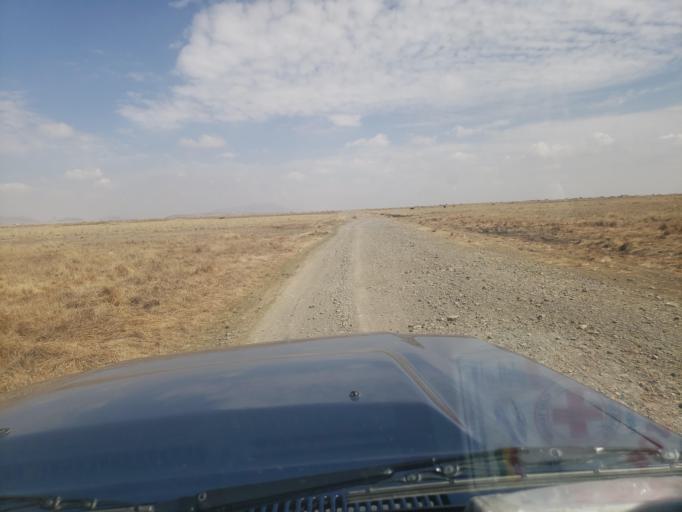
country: BO
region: La Paz
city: Batallas
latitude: -16.4255
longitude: -68.4015
